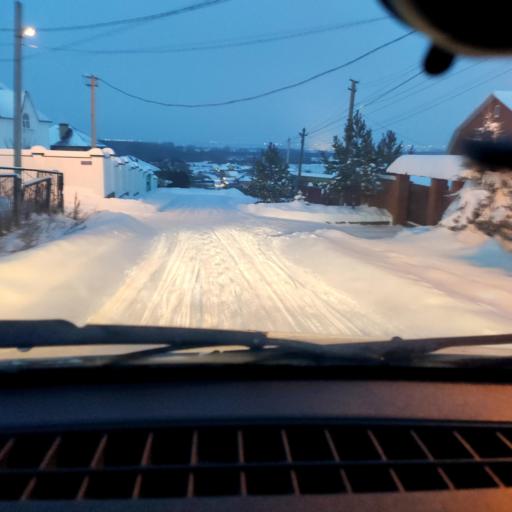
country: RU
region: Bashkortostan
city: Mikhaylovka
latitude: 54.8186
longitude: 55.9021
